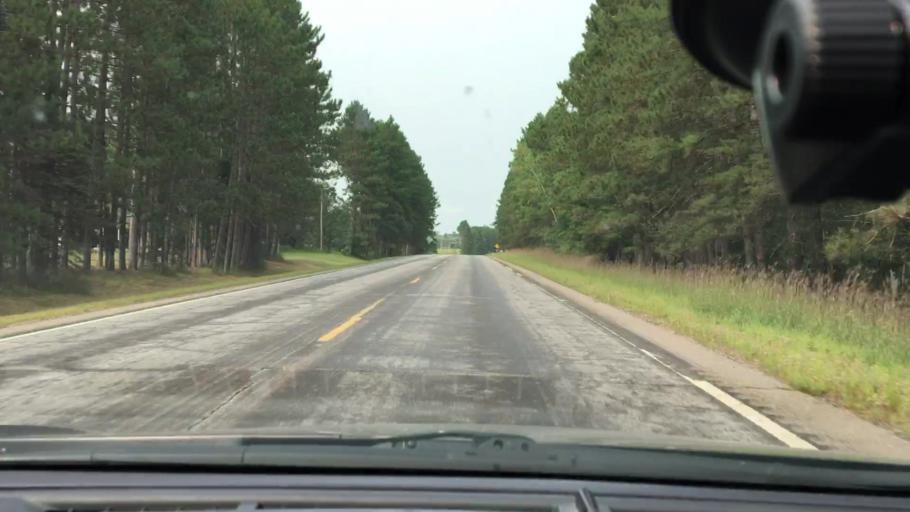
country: US
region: Minnesota
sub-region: Crow Wing County
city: Cross Lake
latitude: 46.7502
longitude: -93.9670
